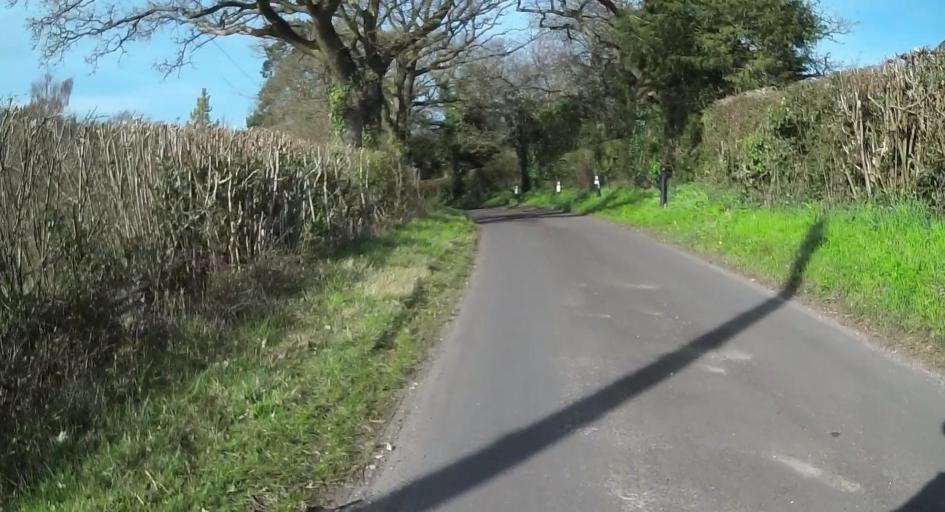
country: GB
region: England
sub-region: Hampshire
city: Highclere
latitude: 51.2649
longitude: -1.3776
